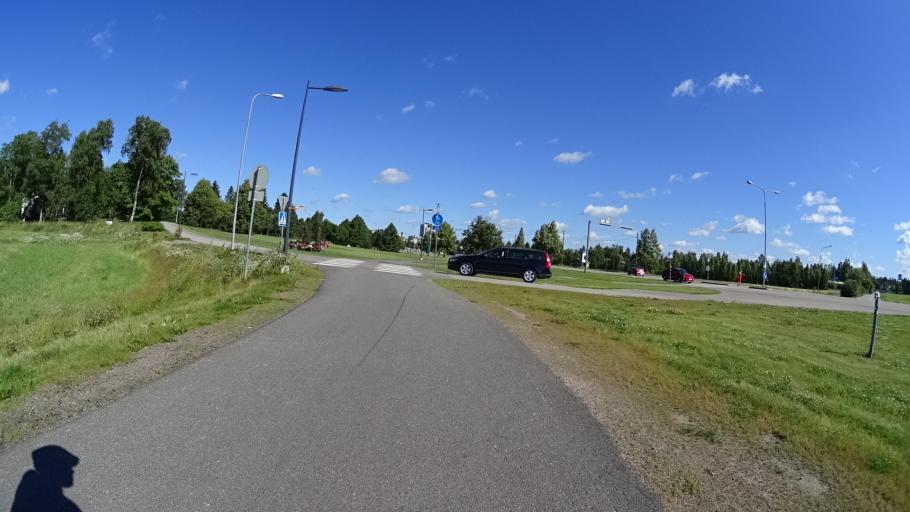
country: FI
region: Uusimaa
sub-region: Helsinki
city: Jaervenpaeae
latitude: 60.4624
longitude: 25.0859
